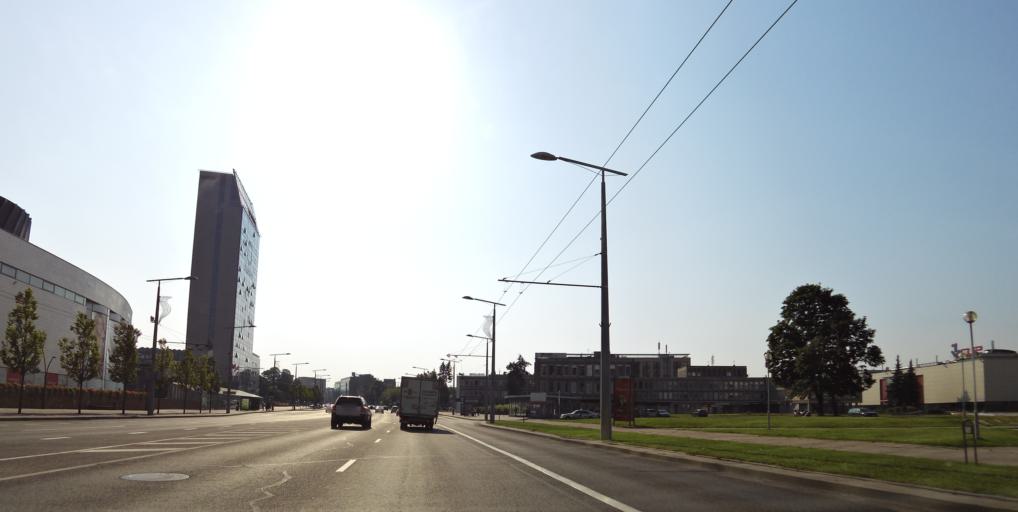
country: LT
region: Vilnius County
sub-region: Vilnius
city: Vilnius
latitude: 54.6959
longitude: 25.2757
